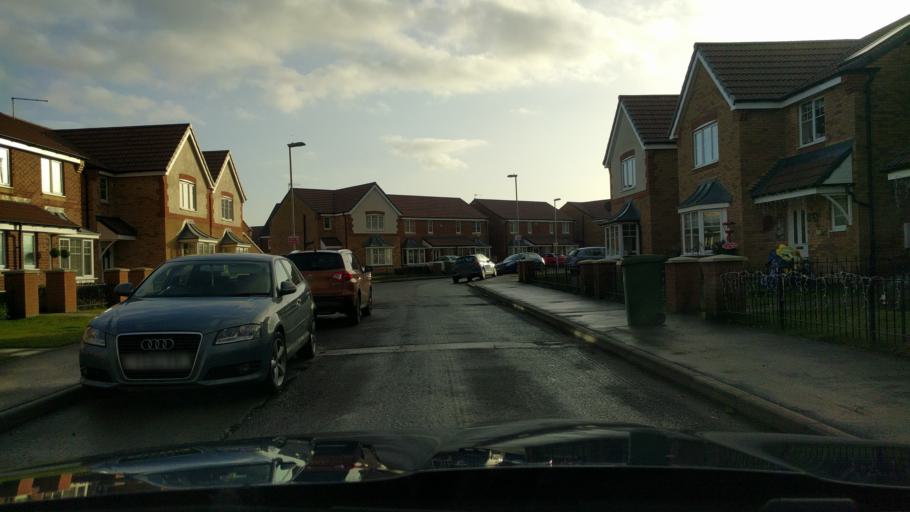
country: GB
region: England
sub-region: Northumberland
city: Ashington
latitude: 55.1872
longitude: -1.5930
